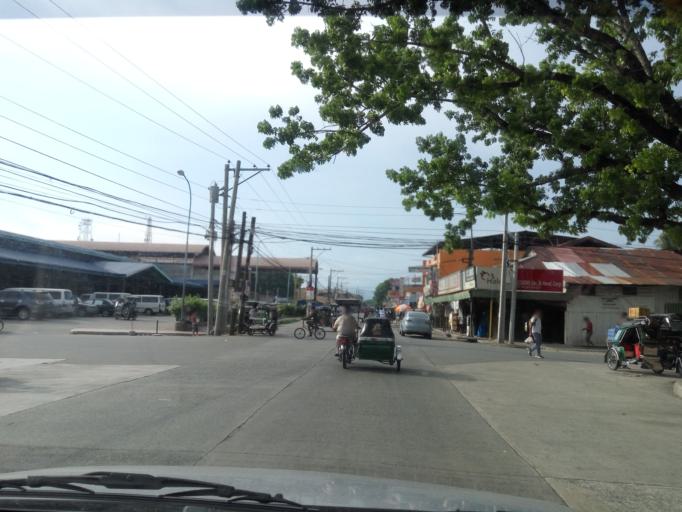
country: PH
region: Ilocos
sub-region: Province of Pangasinan
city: Binalonan
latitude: 16.0468
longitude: 120.5924
